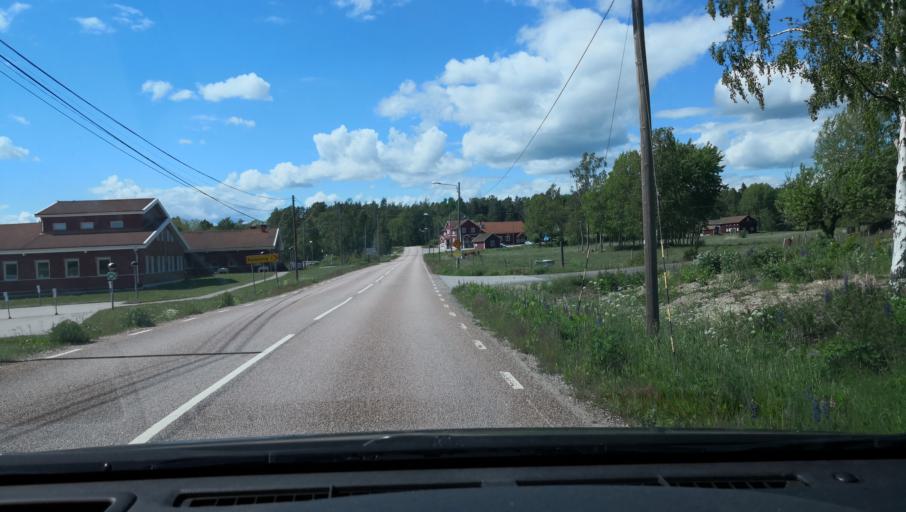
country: SE
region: Vaestmanland
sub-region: Arboga Kommun
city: Tyringe
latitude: 59.2928
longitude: 16.0485
